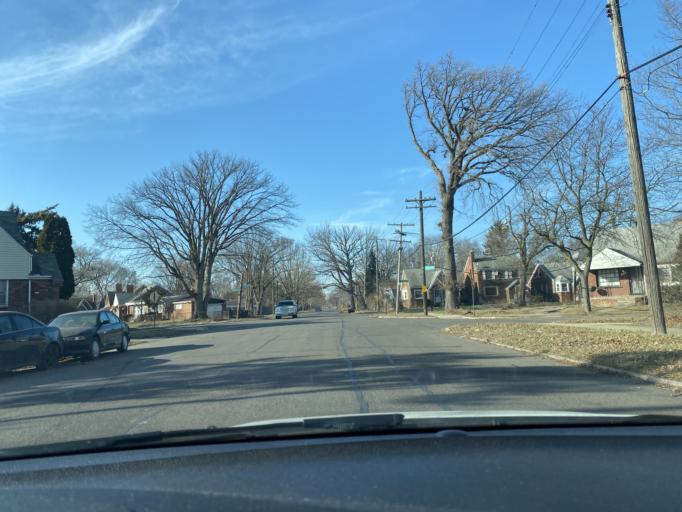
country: US
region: Michigan
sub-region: Wayne County
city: Grosse Pointe Park
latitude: 42.4090
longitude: -82.9508
